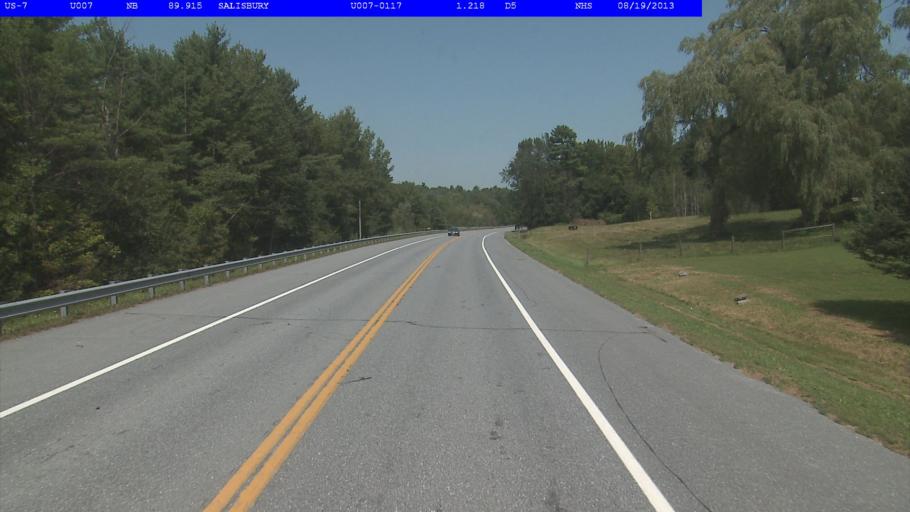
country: US
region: Vermont
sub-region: Rutland County
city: Brandon
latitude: 43.9094
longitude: -73.1110
